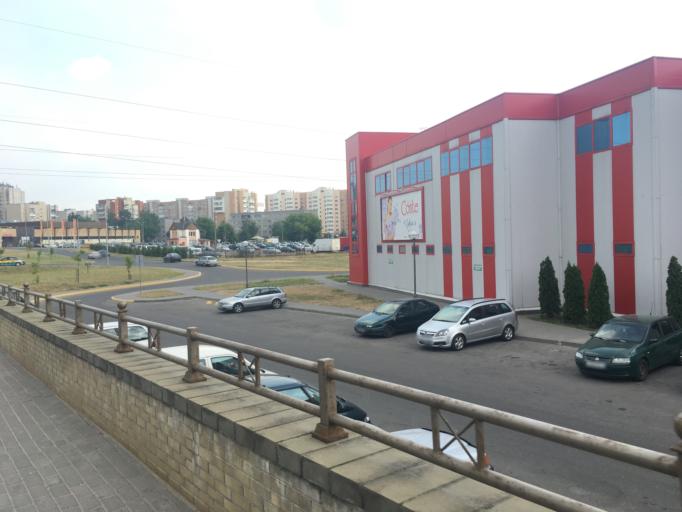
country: BY
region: Grodnenskaya
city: Hrodna
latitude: 53.6531
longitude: 23.8312
